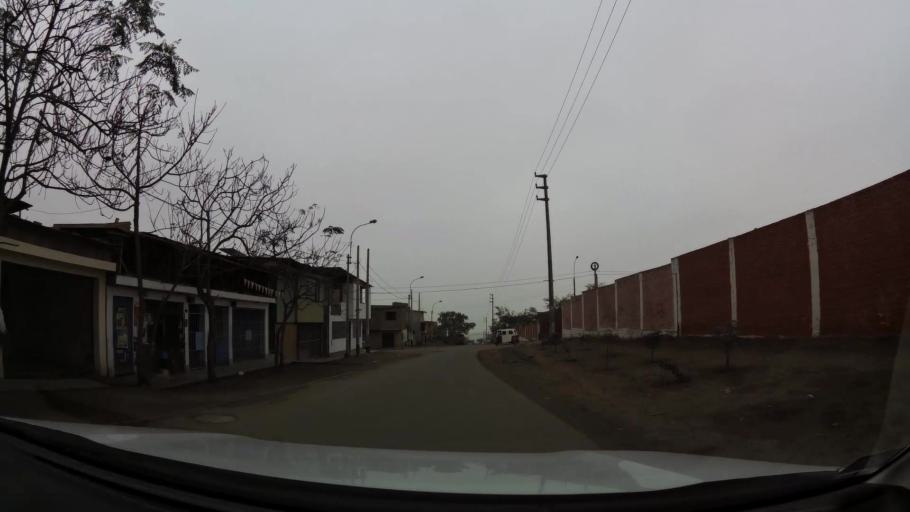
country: PE
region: Lima
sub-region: Lima
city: Surco
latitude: -12.1878
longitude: -76.9285
